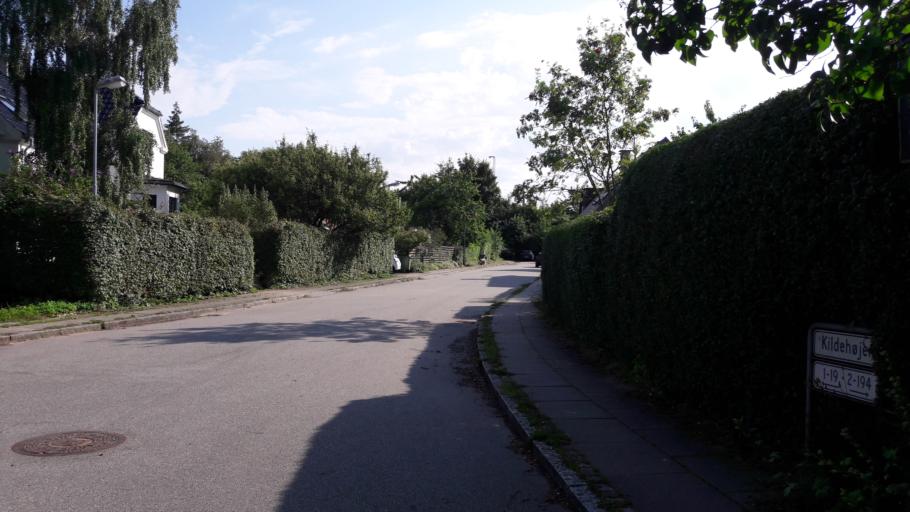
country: DK
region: Central Jutland
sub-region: Arhus Kommune
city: Arhus
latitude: 56.1977
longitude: 10.2180
